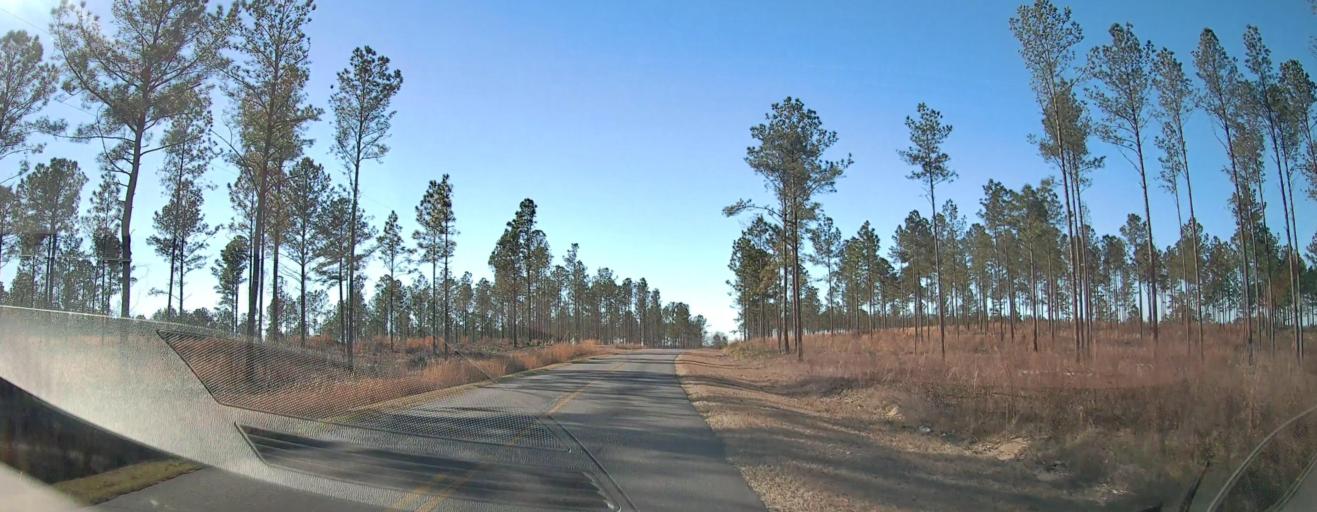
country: US
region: Georgia
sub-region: Taylor County
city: Butler
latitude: 32.6388
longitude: -84.2978
